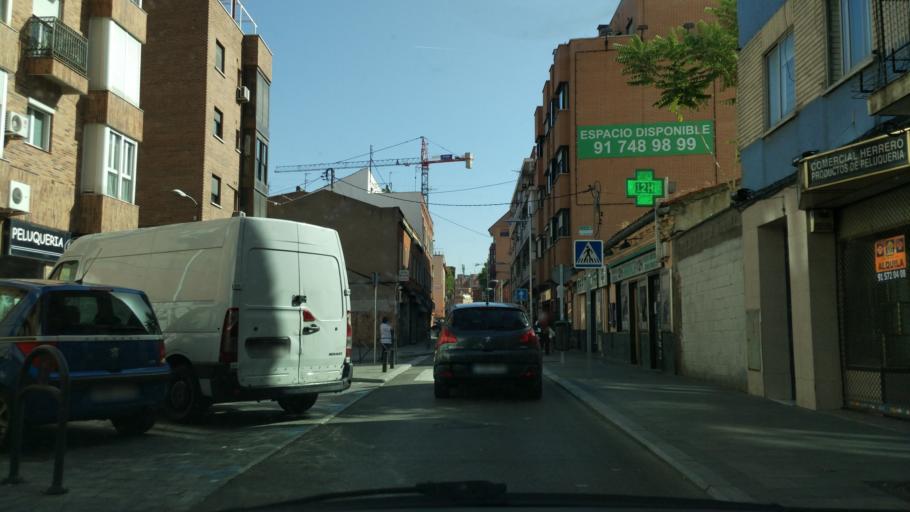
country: ES
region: Madrid
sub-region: Provincia de Madrid
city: Tetuan de las Victorias
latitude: 40.4658
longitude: -3.7004
